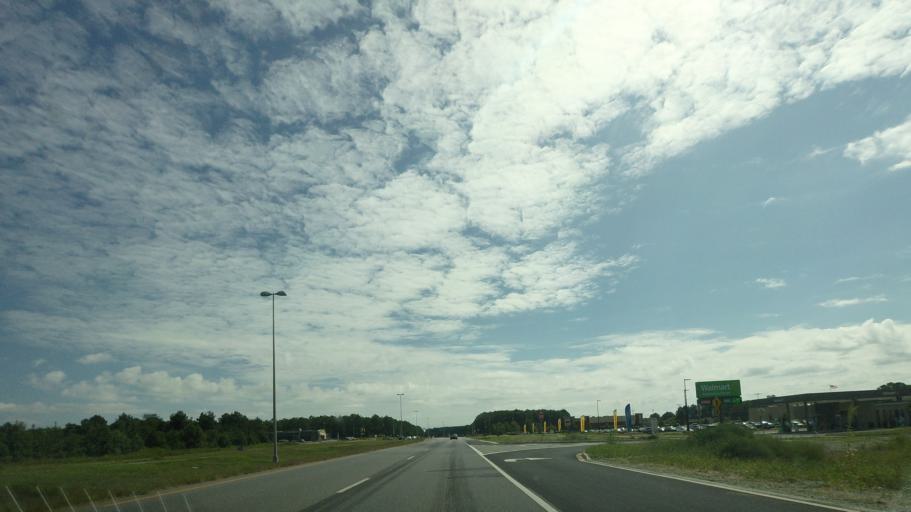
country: US
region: Georgia
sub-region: Houston County
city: Centerville
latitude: 32.5813
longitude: -83.6976
